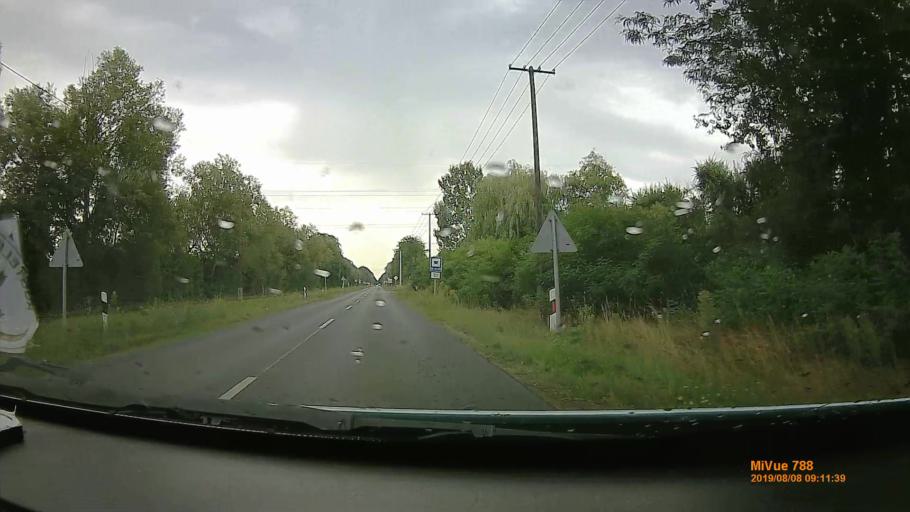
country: HU
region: Hajdu-Bihar
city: Debrecen
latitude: 47.5308
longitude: 21.7062
